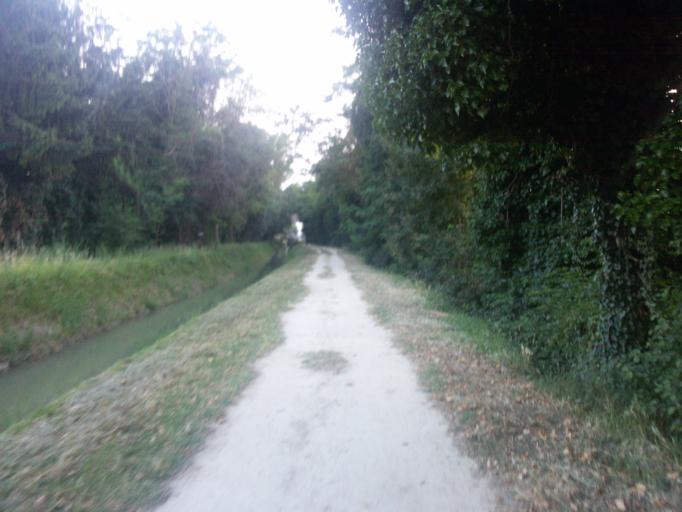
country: IT
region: Emilia-Romagna
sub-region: Provincia di Ravenna
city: Lugo
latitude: 44.4204
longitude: 11.9004
